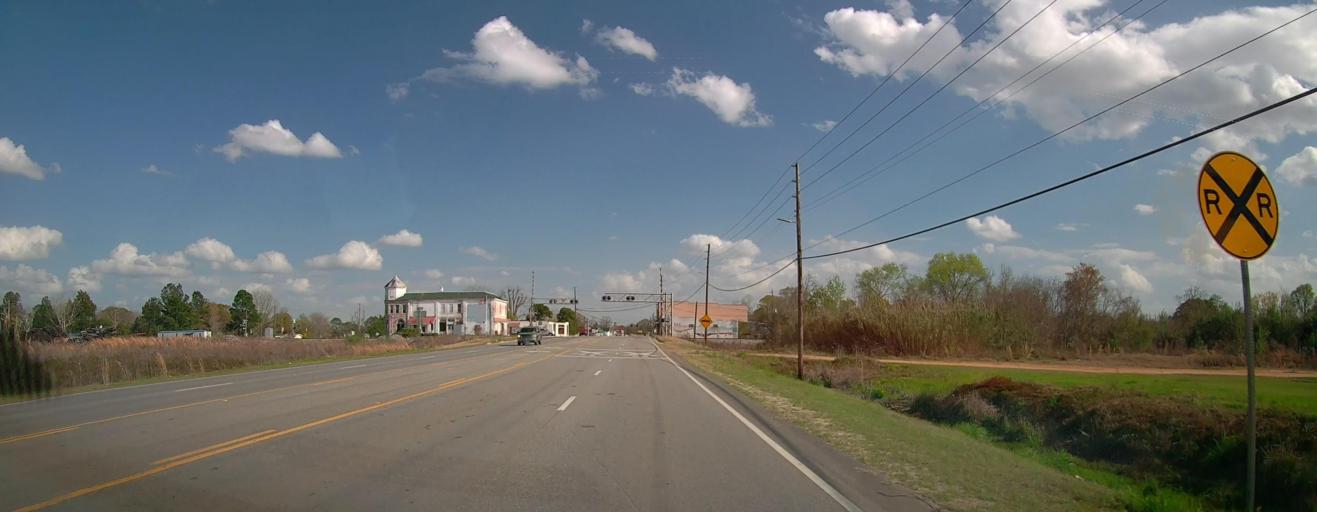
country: US
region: Georgia
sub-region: Telfair County
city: Helena
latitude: 32.0749
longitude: -82.9155
